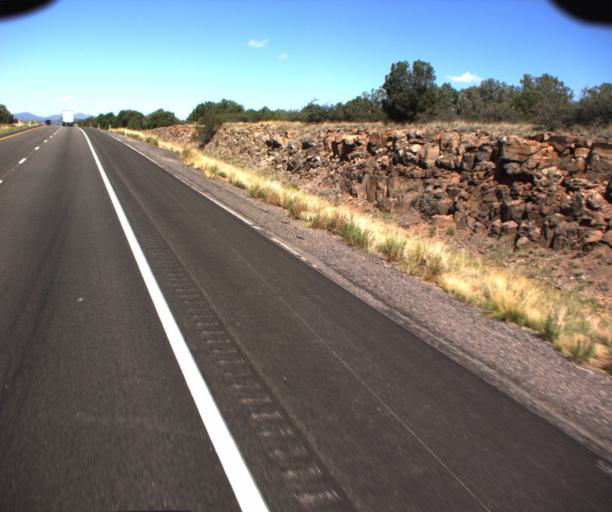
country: US
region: Arizona
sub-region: Mohave County
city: Peach Springs
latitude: 35.1905
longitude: -113.3260
